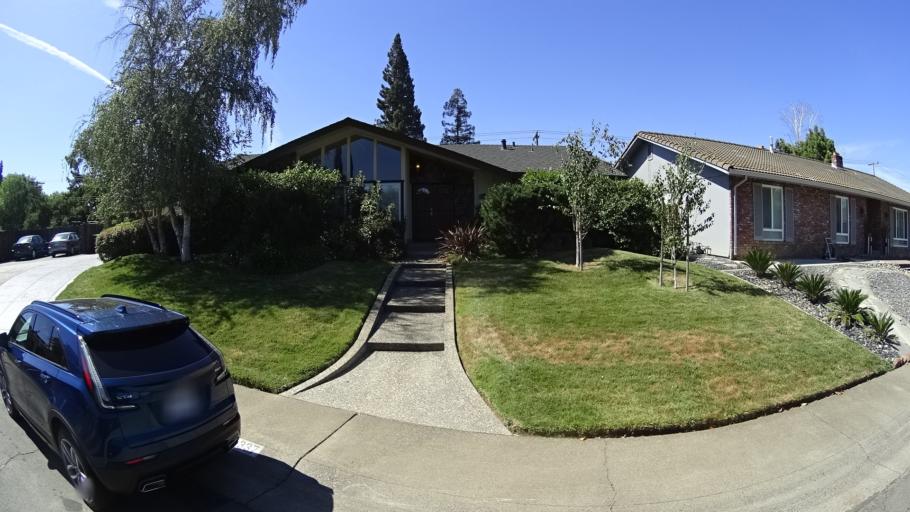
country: US
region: California
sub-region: Sacramento County
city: Parkway
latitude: 38.5035
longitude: -121.5134
